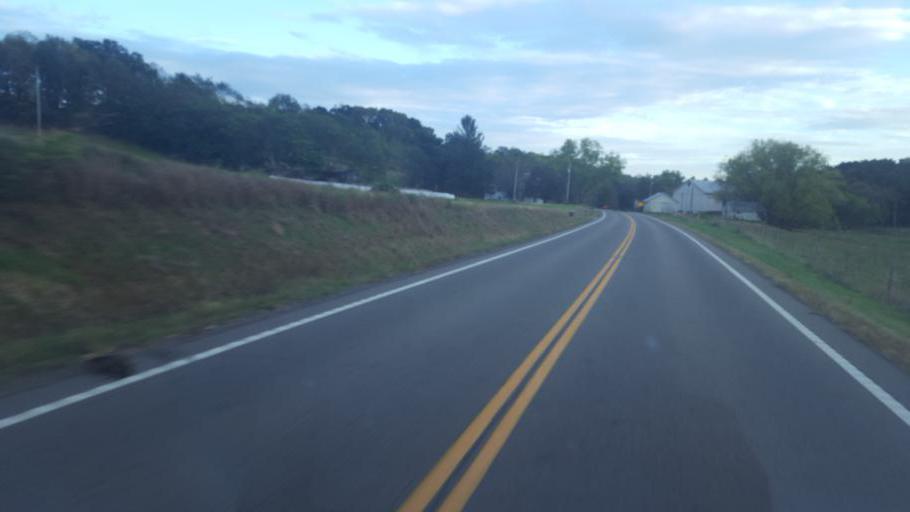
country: US
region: Ohio
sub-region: Ashland County
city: Loudonville
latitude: 40.6744
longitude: -82.2364
